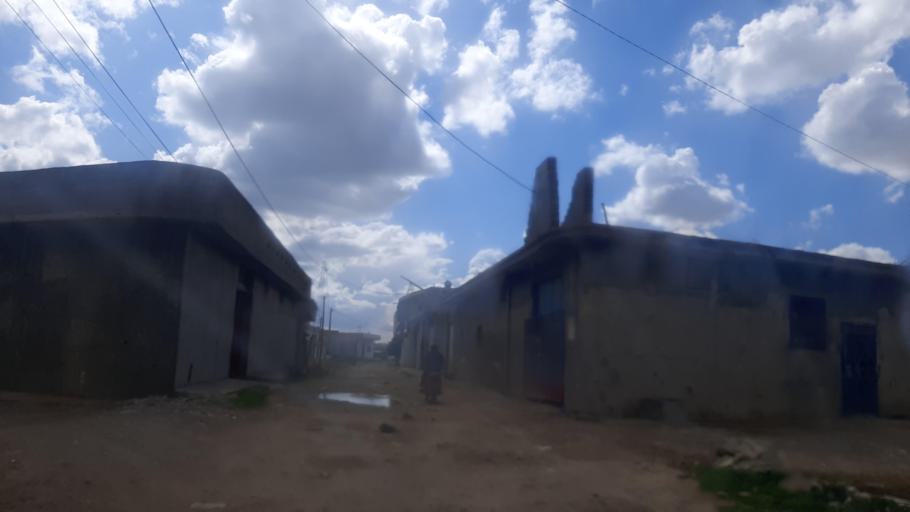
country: TN
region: Nabul
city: Korba
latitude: 36.5908
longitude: 10.8562
